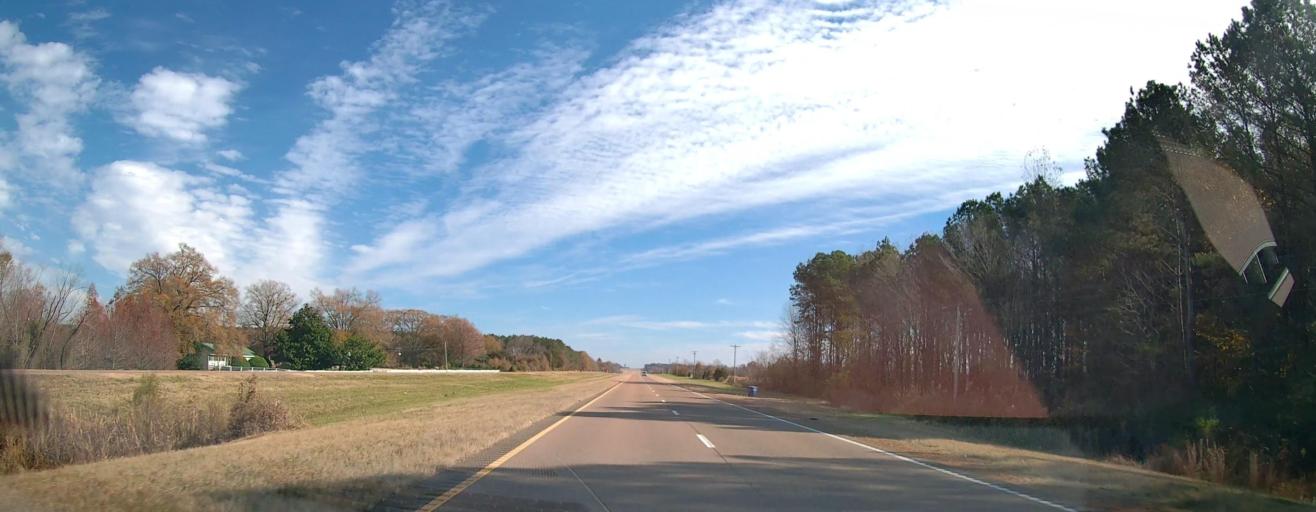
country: US
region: Mississippi
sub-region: Benton County
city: Ashland
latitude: 34.9463
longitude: -89.2237
